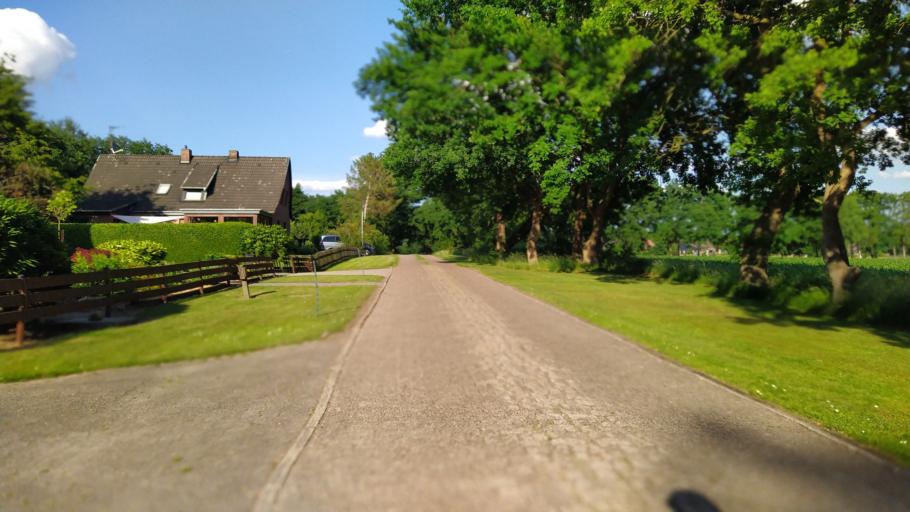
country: DE
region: Lower Saxony
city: Lintig
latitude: 53.5979
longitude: 8.9199
